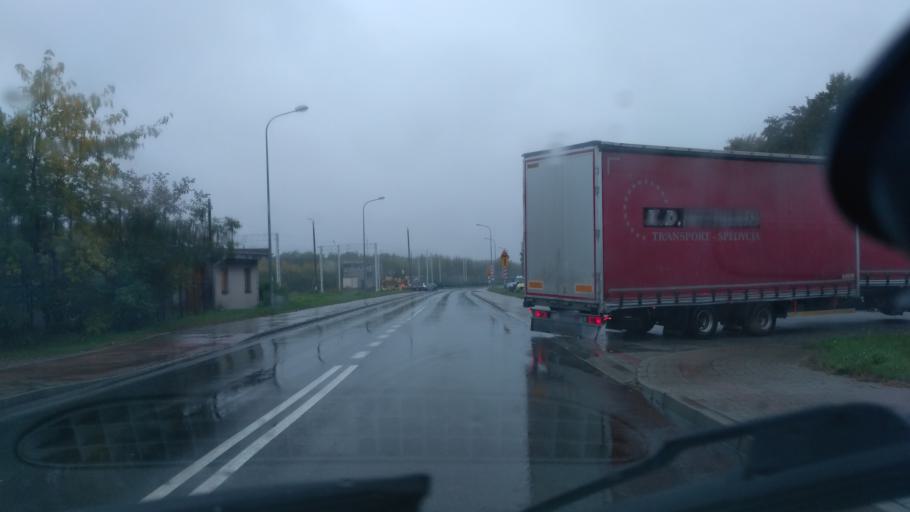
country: PL
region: Subcarpathian Voivodeship
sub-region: Powiat debicki
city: Debica
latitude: 50.0647
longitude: 21.4320
